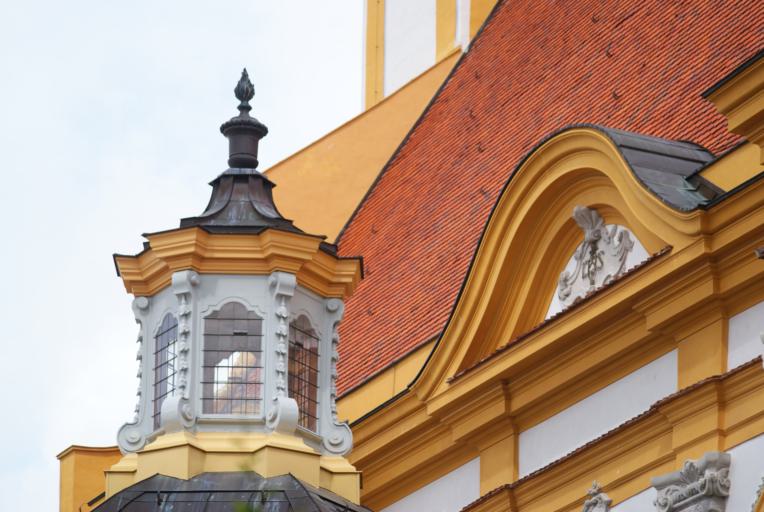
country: DE
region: Brandenburg
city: Neuzelle
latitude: 52.0907
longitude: 14.6538
